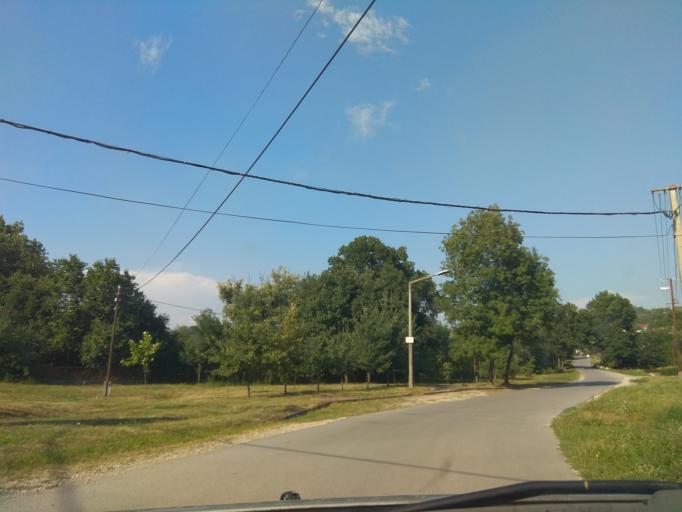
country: HU
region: Borsod-Abauj-Zemplen
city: Emod
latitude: 47.9412
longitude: 20.8116
